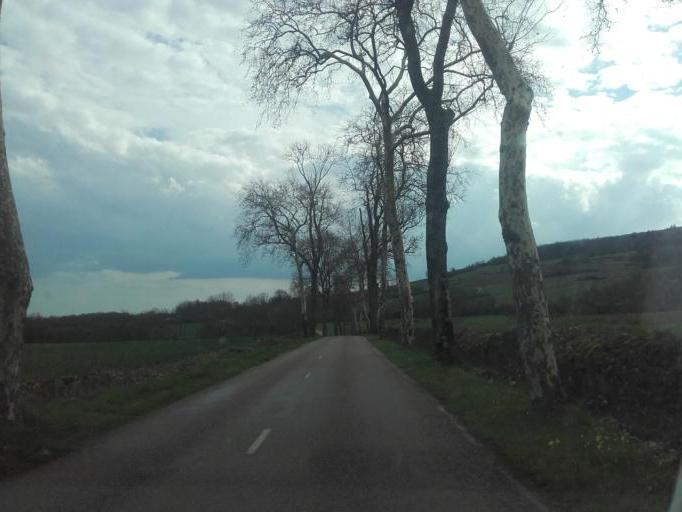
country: FR
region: Bourgogne
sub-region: Departement de la Cote-d'Or
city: Nolay
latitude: 46.9431
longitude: 4.6225
